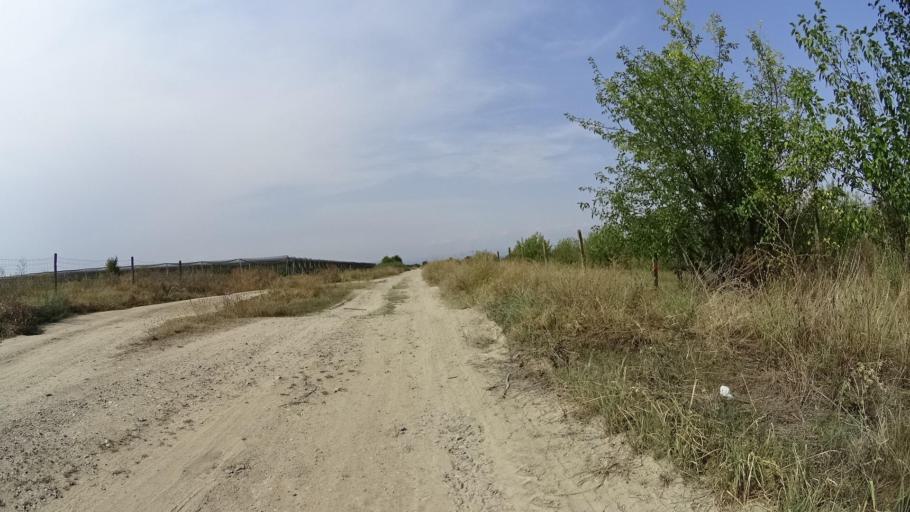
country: BG
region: Plovdiv
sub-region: Obshtina Kaloyanovo
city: Kaloyanovo
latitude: 42.2786
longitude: 24.7995
